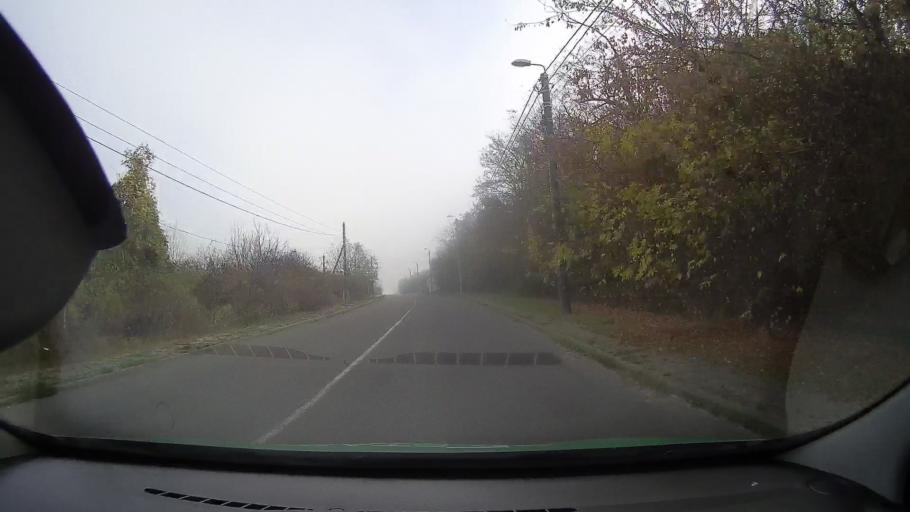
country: RO
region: Tulcea
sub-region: Municipiul Tulcea
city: Tulcea
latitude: 45.1657
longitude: 28.8280
